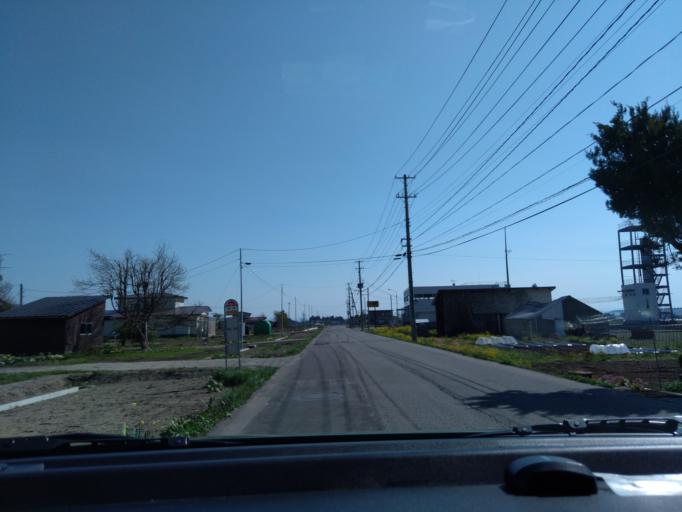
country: JP
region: Akita
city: Kakunodatemachi
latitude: 39.4847
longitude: 140.5909
